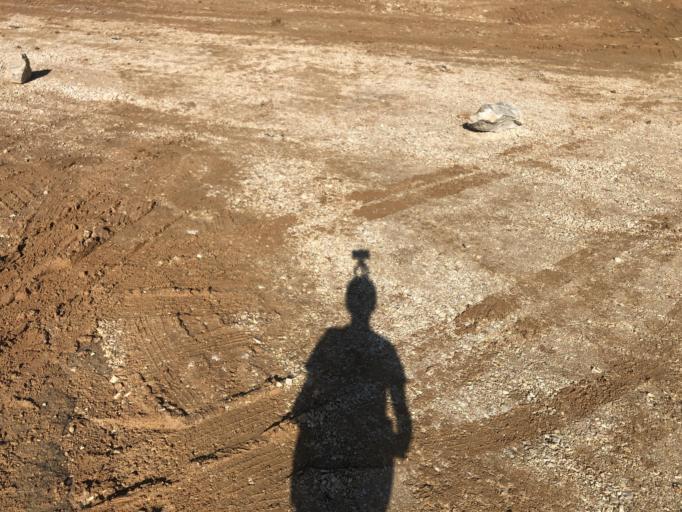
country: IL
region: Jerusalem
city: Modiin Ilit
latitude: 31.9246
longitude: 35.0495
